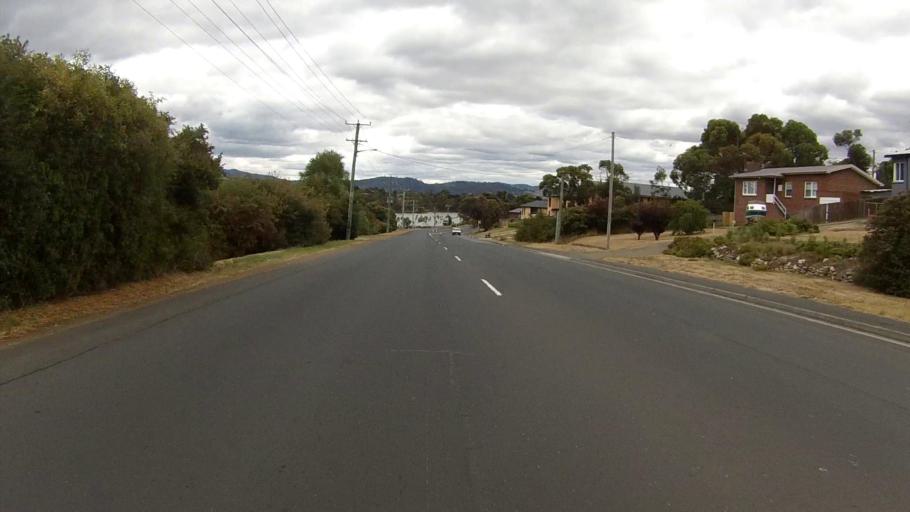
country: AU
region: Tasmania
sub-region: Glenorchy
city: Austins Ferry
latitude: -42.7681
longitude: 147.2447
